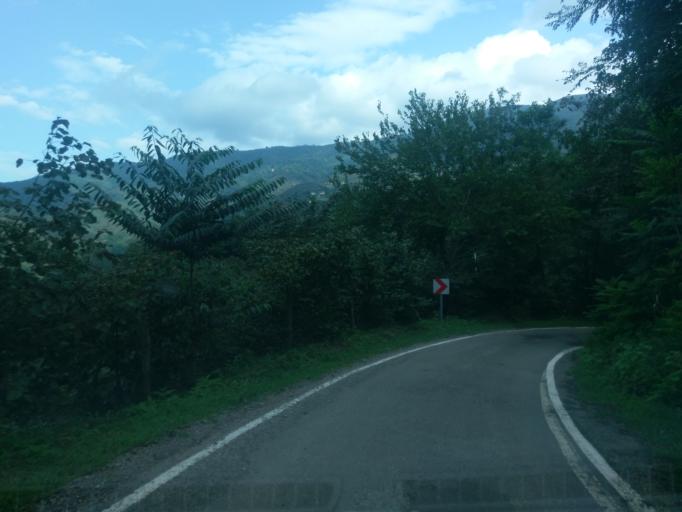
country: TR
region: Ordu
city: Camas
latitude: 40.9346
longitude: 37.6205
